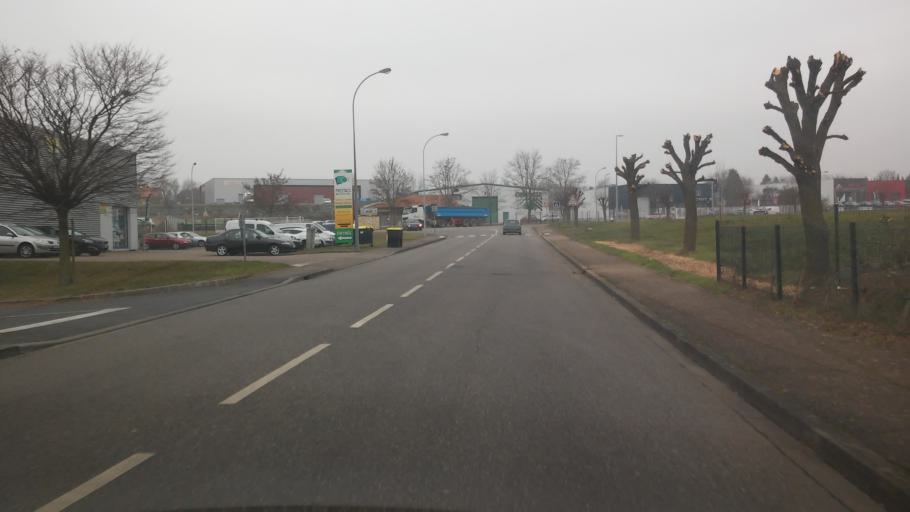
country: FR
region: Lorraine
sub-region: Departement de la Moselle
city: Marly
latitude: 49.0683
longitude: 6.1406
